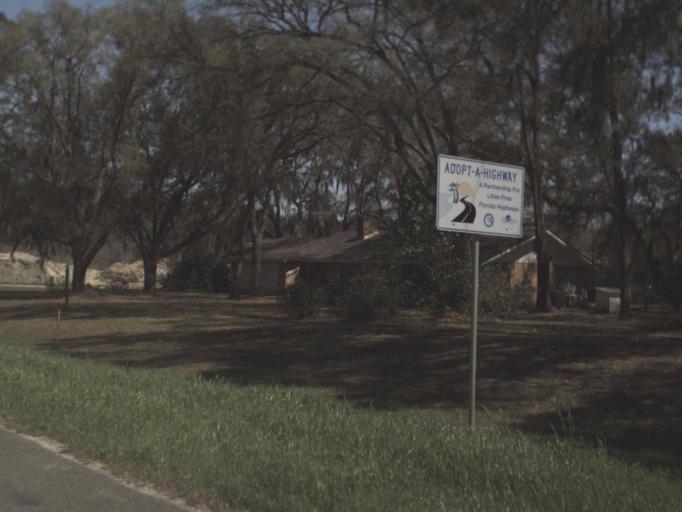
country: US
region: Florida
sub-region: Calhoun County
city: Blountstown
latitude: 30.4351
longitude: -85.0848
